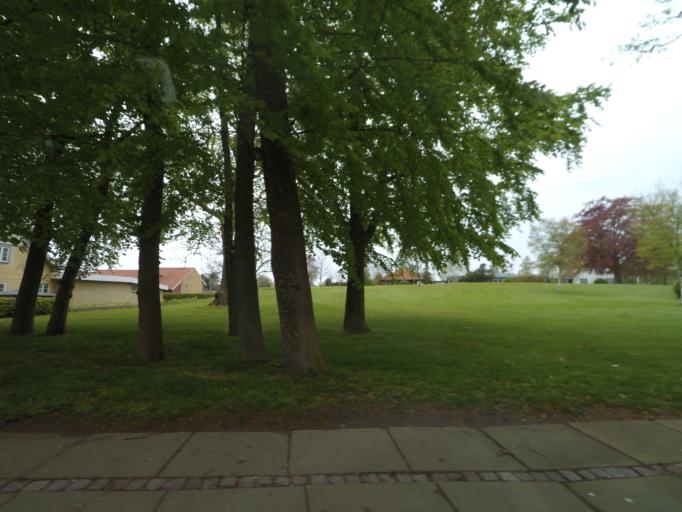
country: DK
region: South Denmark
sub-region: Svendborg Kommune
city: Thuro By
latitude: 55.1509
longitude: 10.7079
